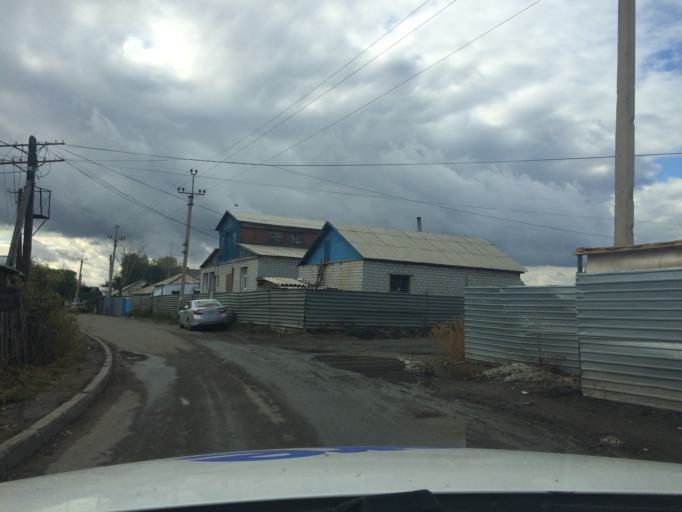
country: KZ
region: Astana Qalasy
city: Astana
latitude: 51.1869
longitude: 71.4010
